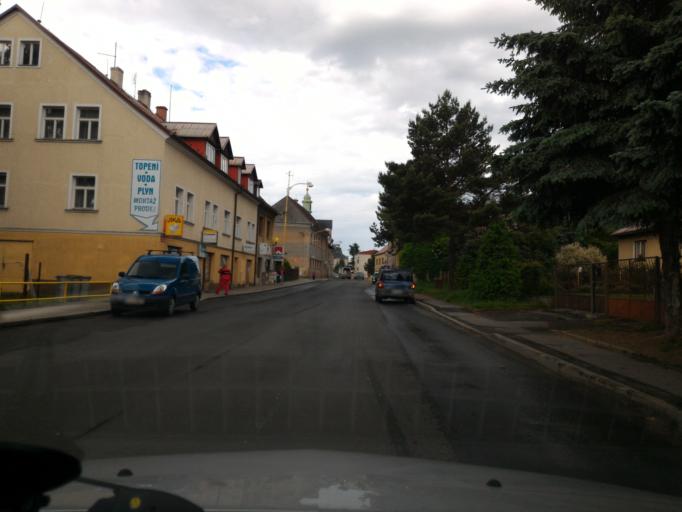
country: CZ
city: Jablonne v Podjestedi
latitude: 50.7688
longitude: 14.7660
